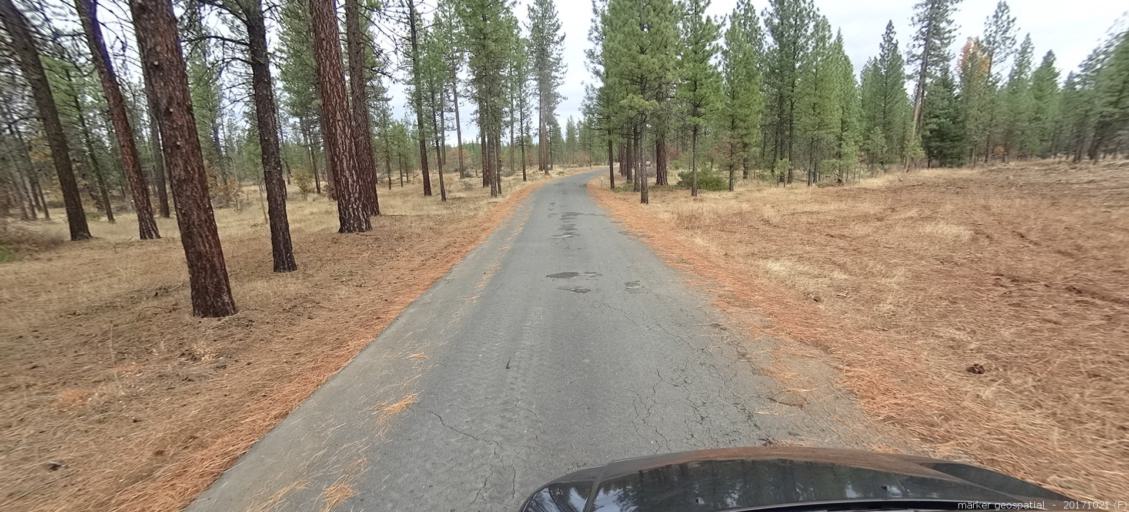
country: US
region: California
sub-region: Shasta County
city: Burney
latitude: 40.9923
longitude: -121.6332
